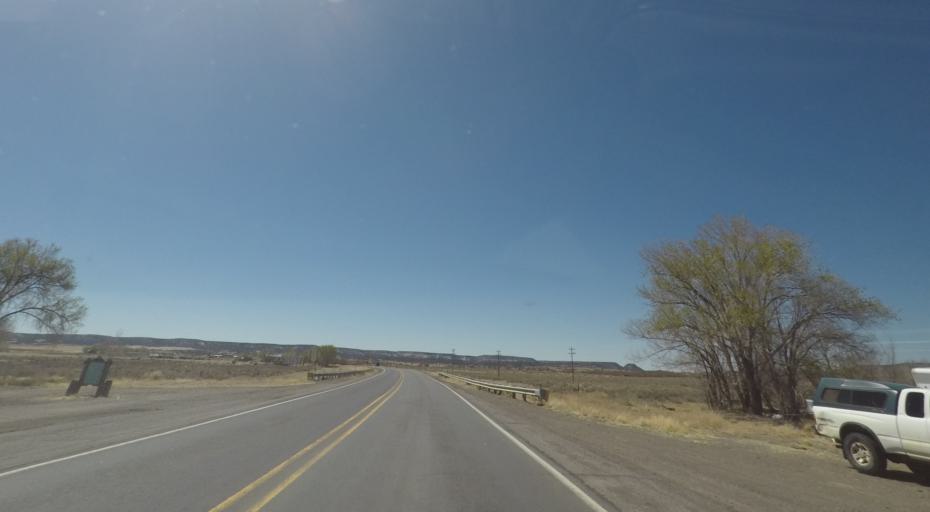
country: US
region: New Mexico
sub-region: Catron County
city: Reserve
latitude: 34.3441
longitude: -108.5004
